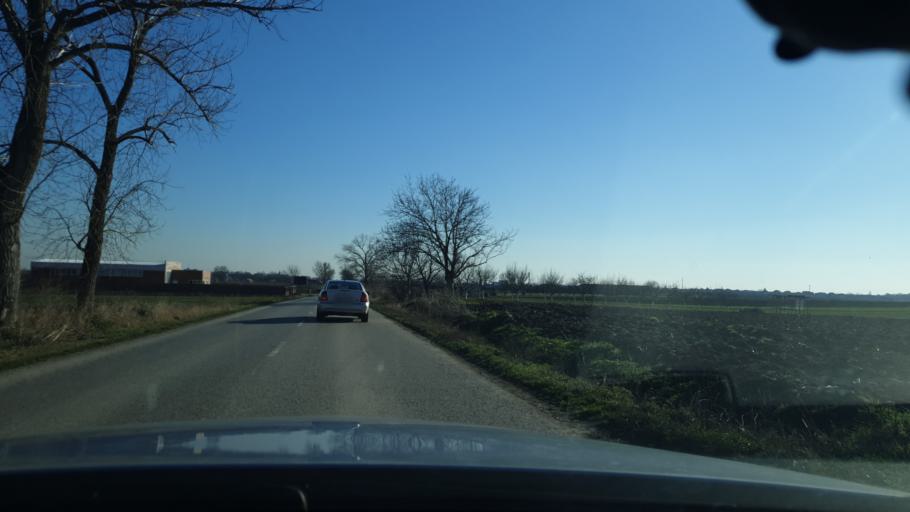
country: RS
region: Autonomna Pokrajina Vojvodina
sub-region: Sremski Okrug
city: Ruma
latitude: 45.0282
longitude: 19.8117
